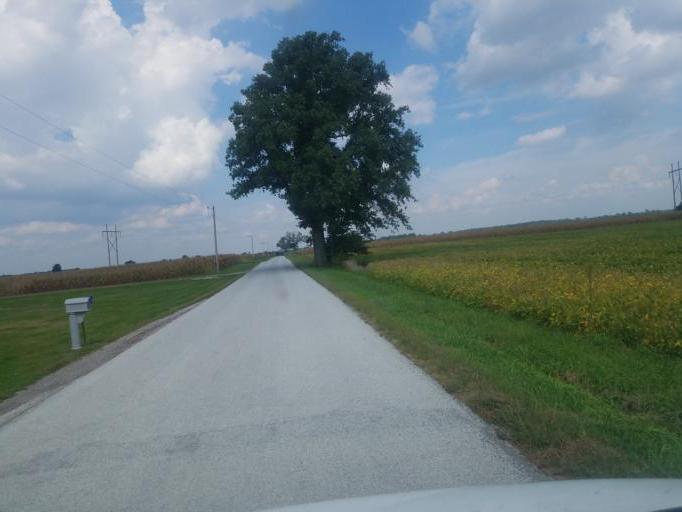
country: US
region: Ohio
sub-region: Hardin County
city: Kenton
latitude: 40.6302
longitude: -83.6526
